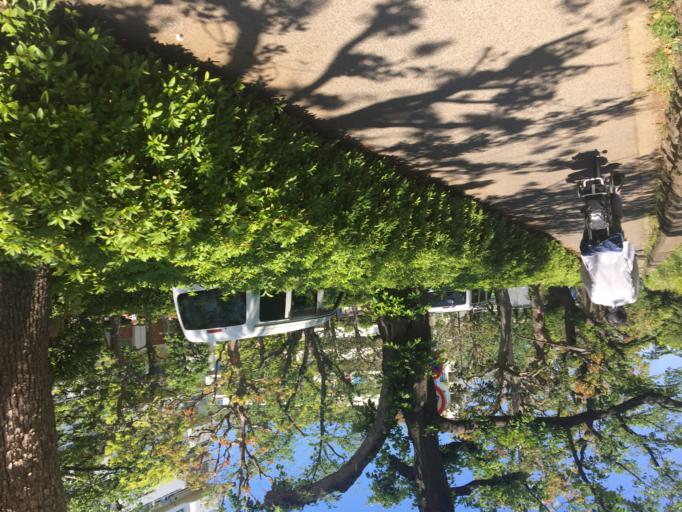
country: JP
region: Saitama
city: Wako
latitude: 35.7678
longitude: 139.6354
